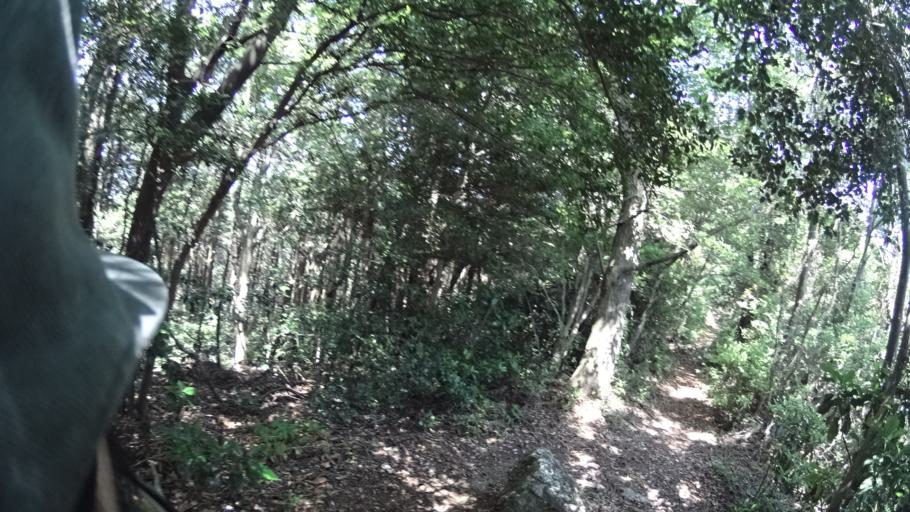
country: JP
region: Shizuoka
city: Kosai-shi
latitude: 34.7836
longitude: 137.4858
